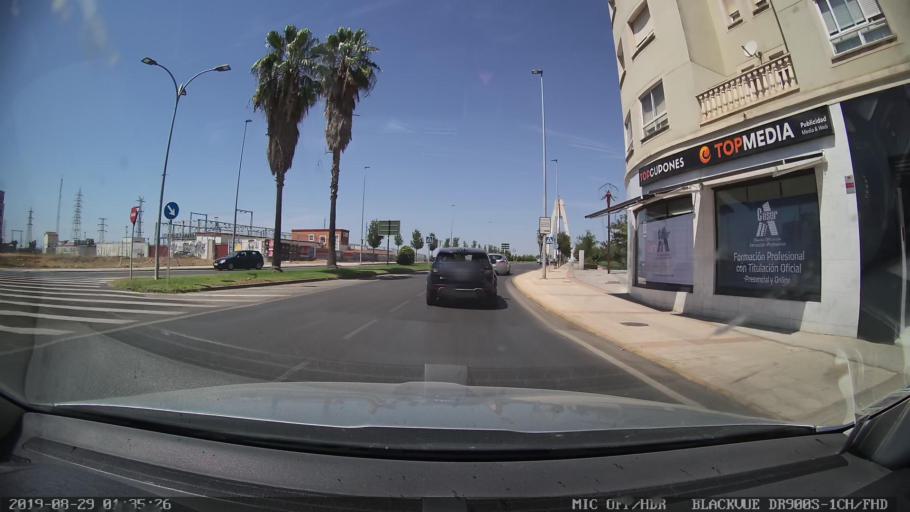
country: ES
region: Extremadura
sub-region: Provincia de Badajoz
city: Badajoz
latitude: 38.8723
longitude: -6.9899
